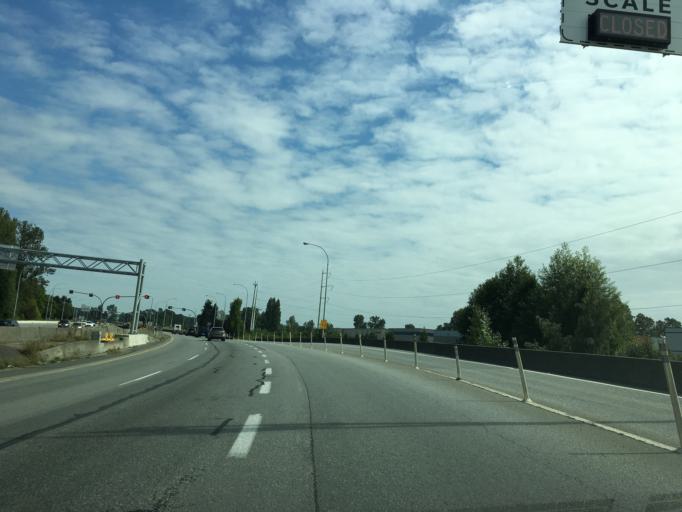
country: CA
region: British Columbia
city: Ladner
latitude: 49.1310
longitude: -123.0867
